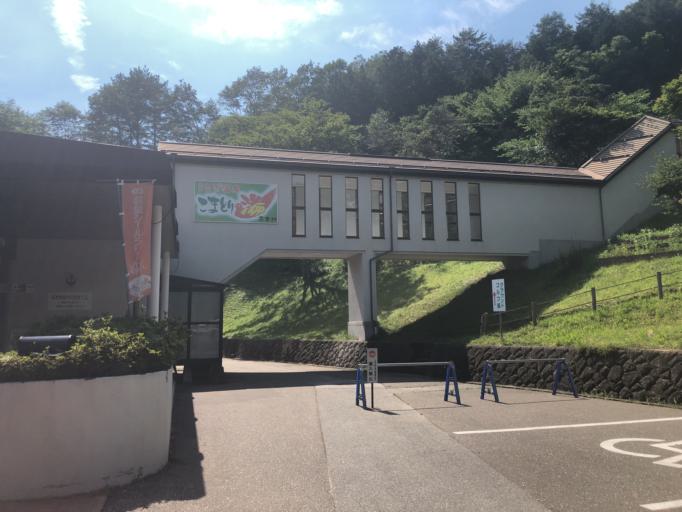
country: JP
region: Nagano
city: Iida
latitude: 35.2765
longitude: 137.7097
